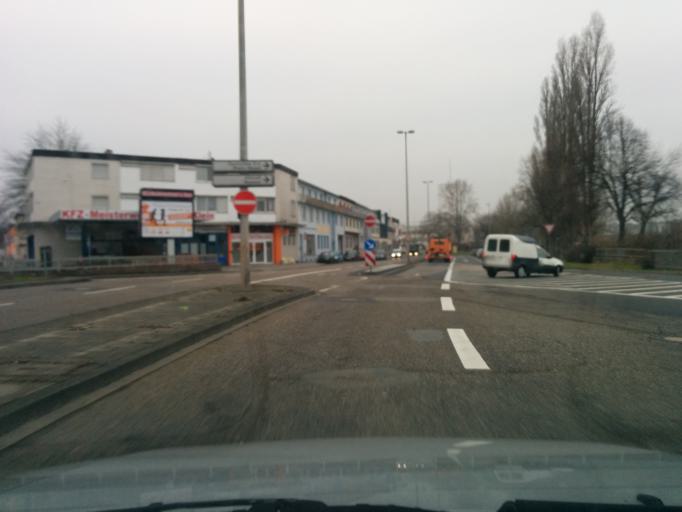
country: DE
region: Rheinland-Pfalz
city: Koblenz
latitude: 50.3630
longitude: 7.5854
